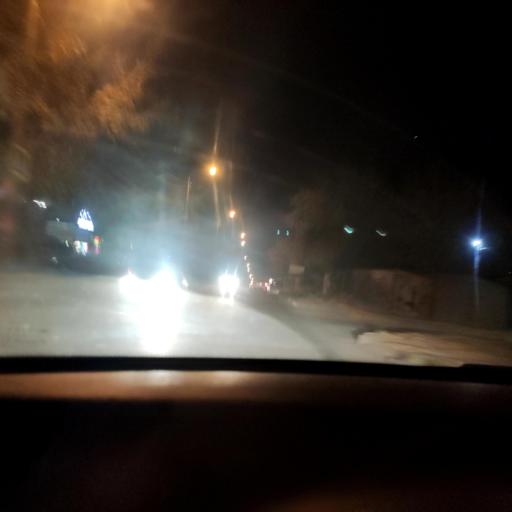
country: RU
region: Samara
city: Samara
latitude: 53.1873
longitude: 50.1875
